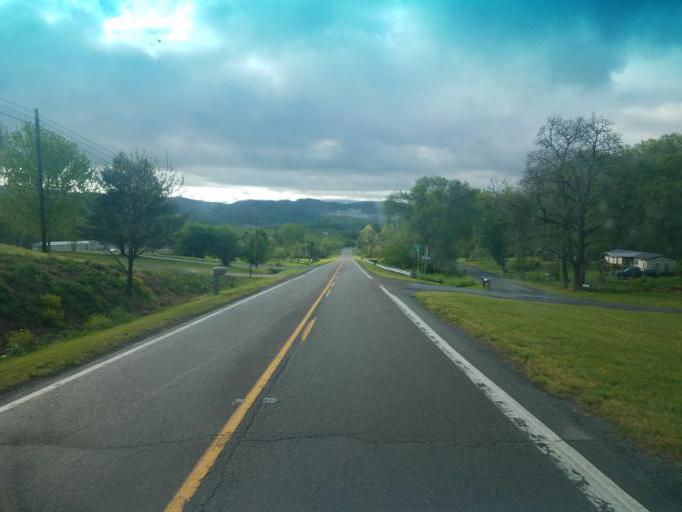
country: US
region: Virginia
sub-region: Washington County
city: Emory
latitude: 36.6797
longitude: -81.8136
